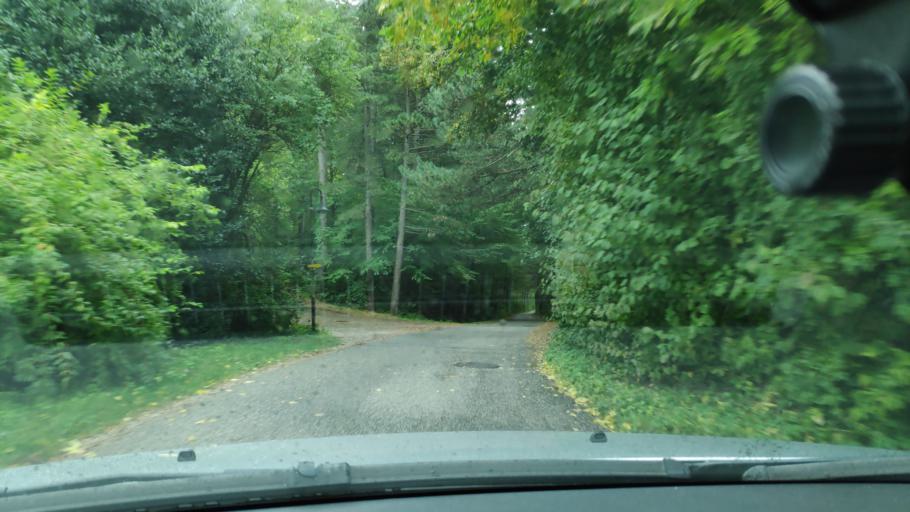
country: AT
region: Lower Austria
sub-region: Politischer Bezirk Neunkirchen
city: Grunbach am Schneeberg
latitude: 47.8040
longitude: 15.9918
